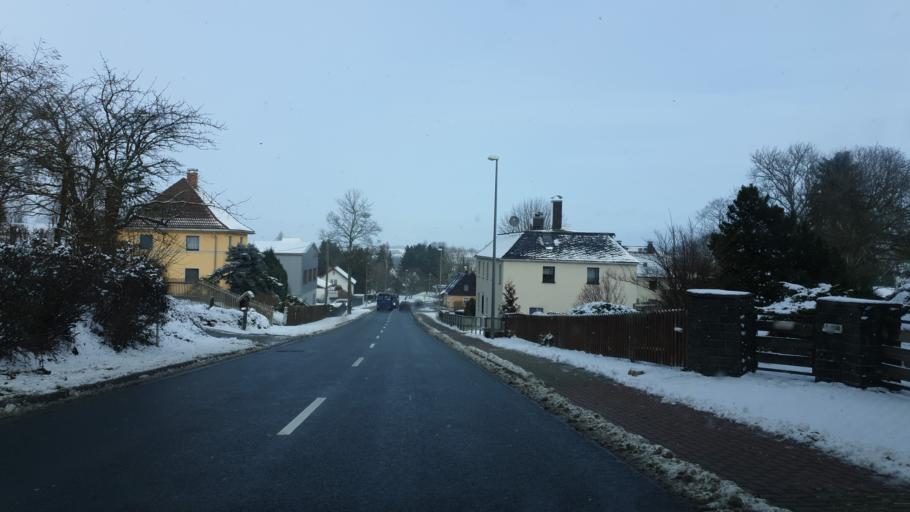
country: DE
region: Saxony
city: Oelsnitz
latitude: 50.3928
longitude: 12.1502
